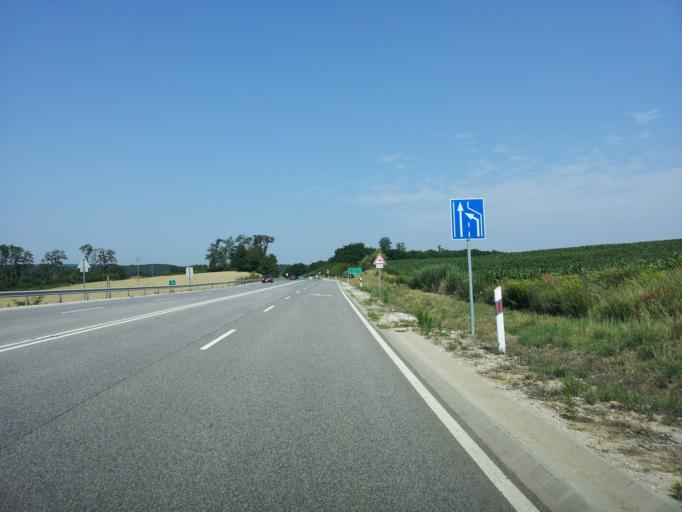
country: HU
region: Zala
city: Pacsa
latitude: 46.8307
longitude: 17.0483
